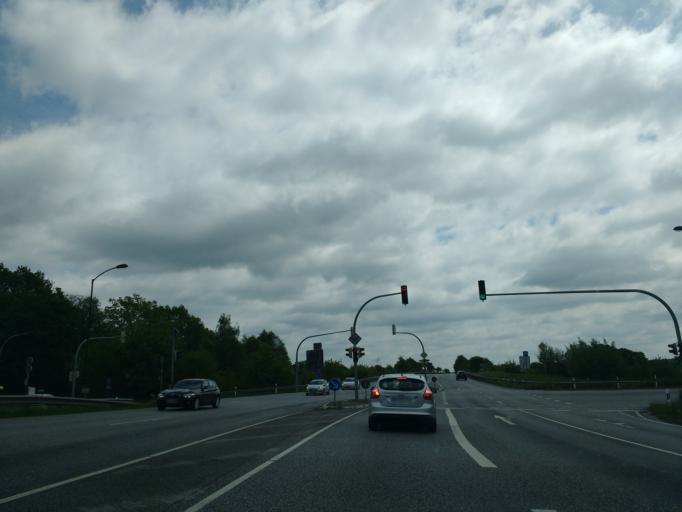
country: DE
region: Schleswig-Holstein
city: Glinde
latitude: 53.5677
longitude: 10.2208
